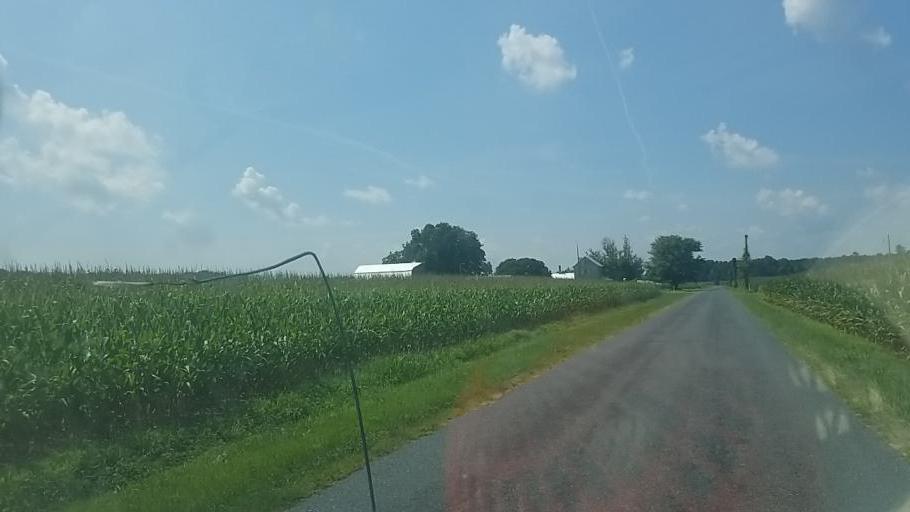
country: US
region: Maryland
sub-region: Worcester County
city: Berlin
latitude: 38.2963
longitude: -75.2923
